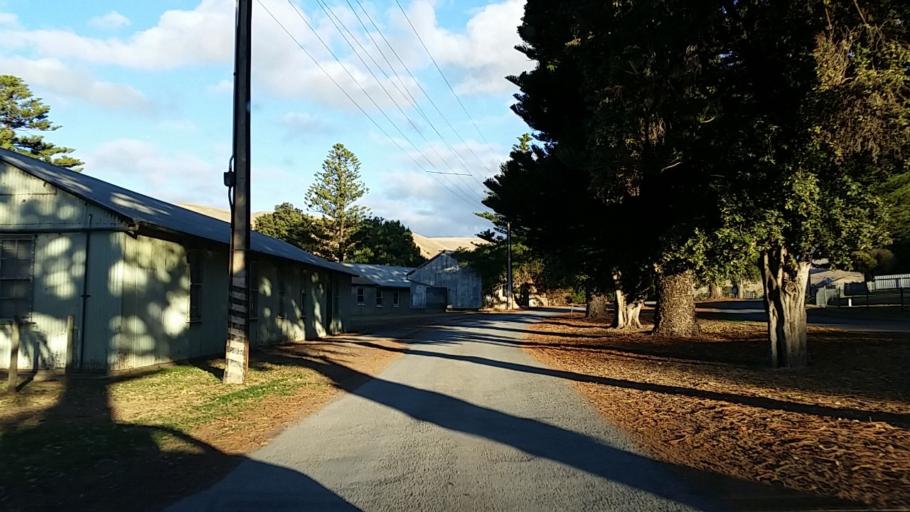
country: AU
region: South Australia
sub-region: Yankalilla
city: Normanville
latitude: -35.5267
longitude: 138.1901
